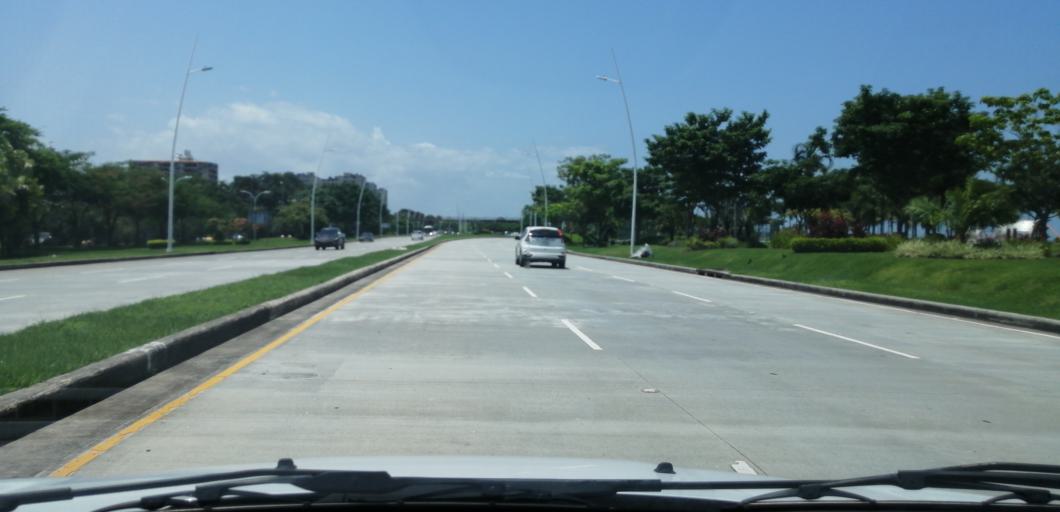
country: PA
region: Panama
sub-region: Distrito de Panama
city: Ancon
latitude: 8.9477
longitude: -79.5458
